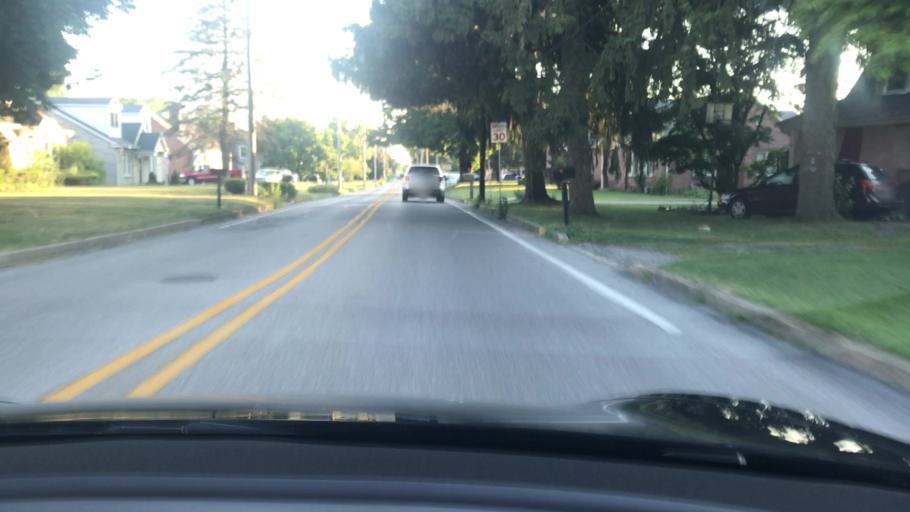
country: US
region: Pennsylvania
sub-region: York County
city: Shiloh
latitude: 39.9757
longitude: -76.7927
